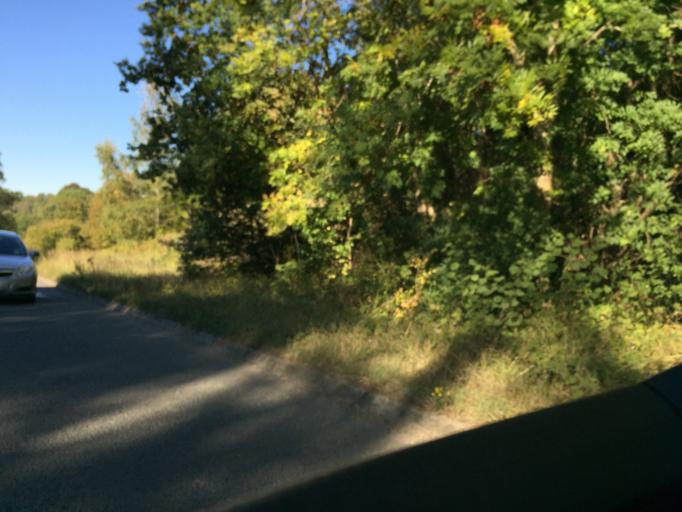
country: GB
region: England
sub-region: Wiltshire
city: Biddestone
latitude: 51.4711
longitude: -2.2115
